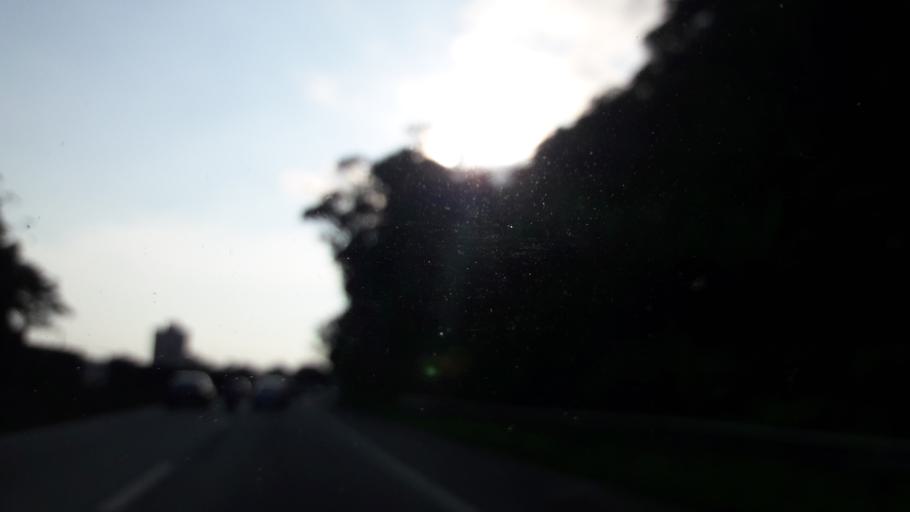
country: BR
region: Sao Paulo
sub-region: Mongagua
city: Mongagua
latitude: -24.0904
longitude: -46.6162
